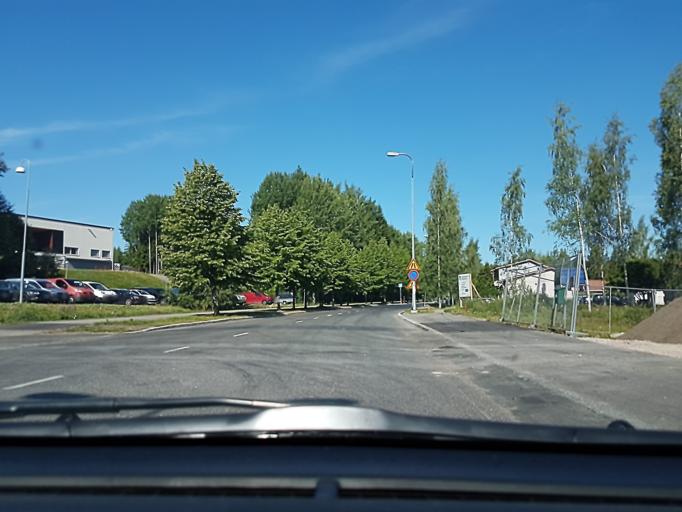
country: FI
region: Uusimaa
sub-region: Helsinki
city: Vantaa
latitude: 60.3354
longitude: 25.0609
